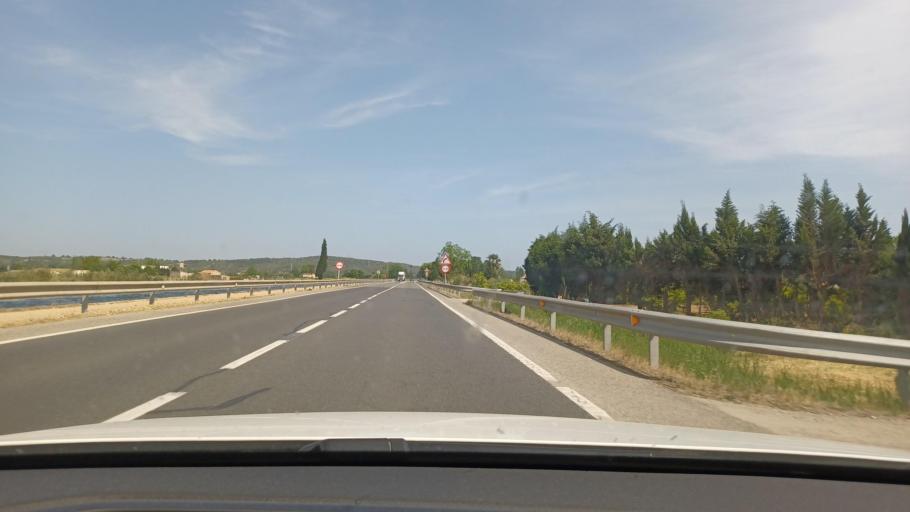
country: ES
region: Catalonia
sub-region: Provincia de Tarragona
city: Masdenverge
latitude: 40.7480
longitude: 0.5549
